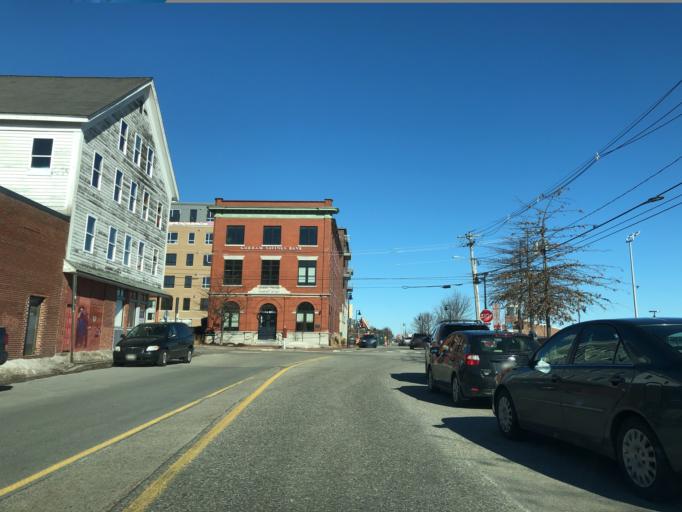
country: US
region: Maine
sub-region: Cumberland County
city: Portland
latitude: 43.6590
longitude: -70.2489
